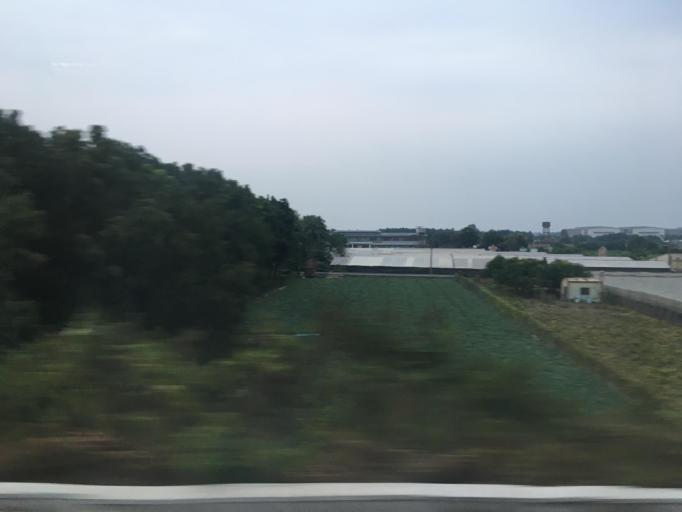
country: TW
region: Taiwan
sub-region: Pingtung
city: Pingtung
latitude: 22.6620
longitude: 120.4465
